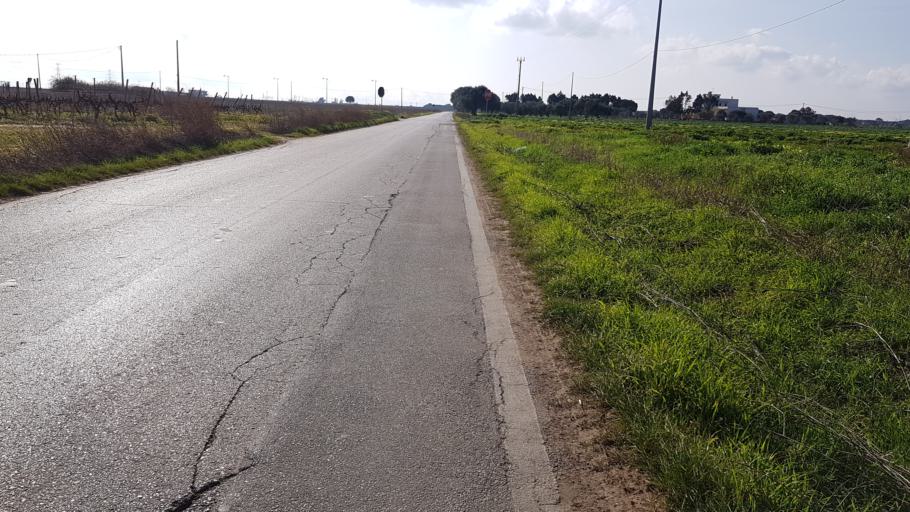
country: IT
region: Apulia
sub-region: Provincia di Brindisi
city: La Rosa
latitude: 40.5820
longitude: 17.9022
